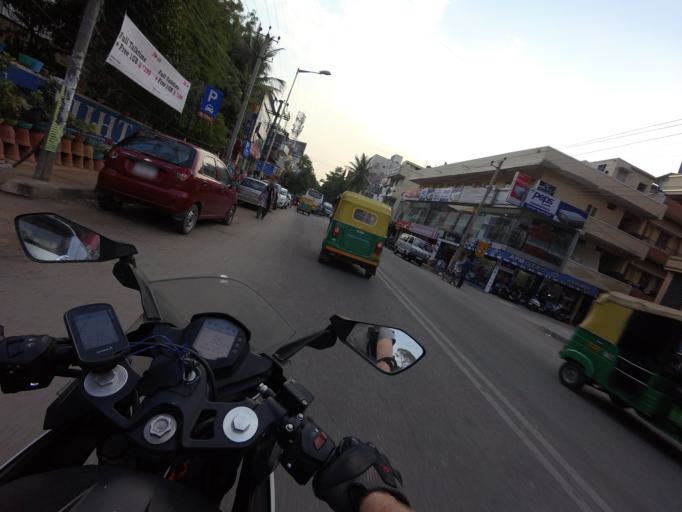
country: IN
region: Karnataka
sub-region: Bangalore Urban
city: Bangalore
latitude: 13.0156
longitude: 77.6360
